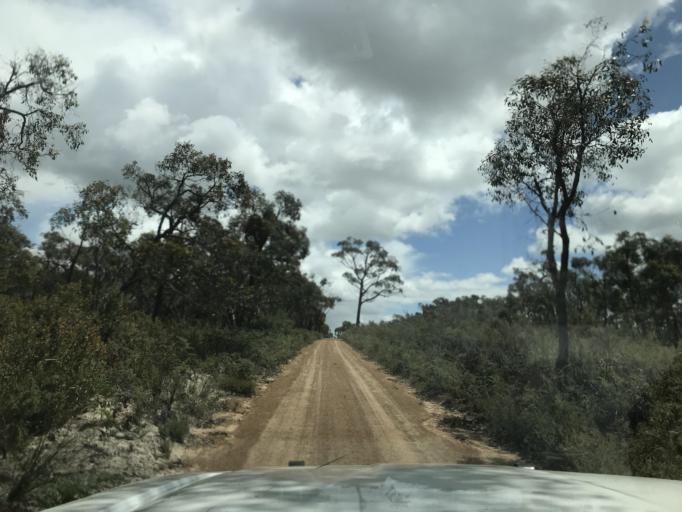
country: AU
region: South Australia
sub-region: Wattle Range
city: Penola
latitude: -37.0895
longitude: 141.3408
